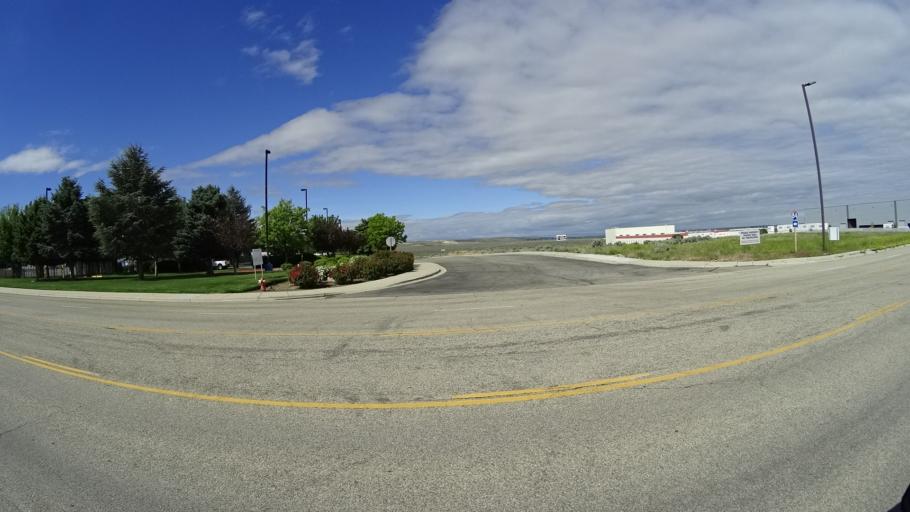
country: US
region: Idaho
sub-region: Ada County
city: Boise
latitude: 43.5384
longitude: -116.1626
